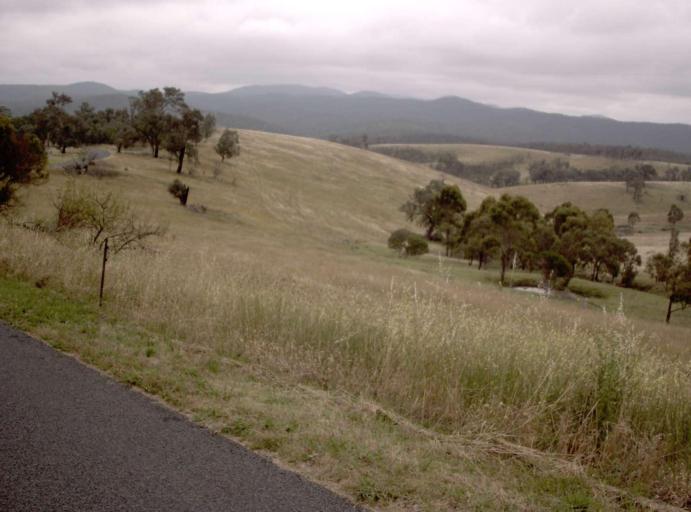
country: AU
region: Victoria
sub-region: Wellington
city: Heyfield
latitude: -37.8687
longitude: 146.7065
